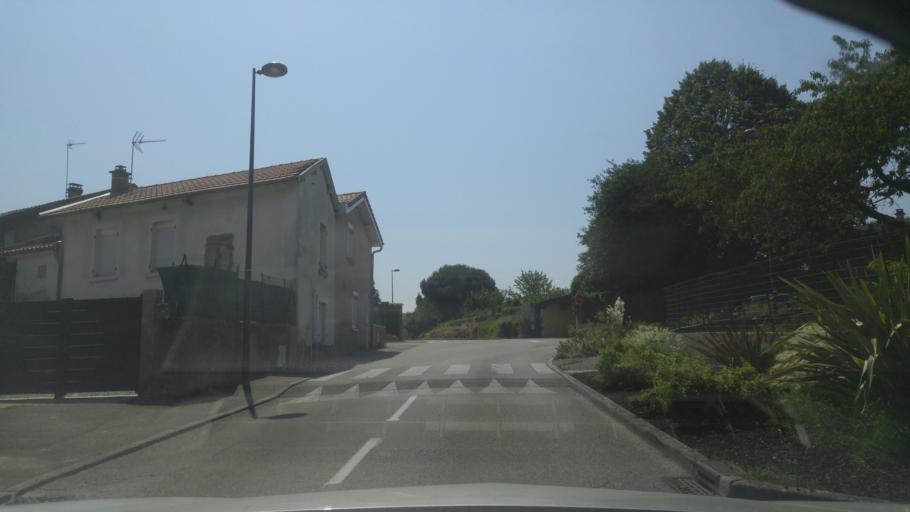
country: FR
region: Rhone-Alpes
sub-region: Departement de l'Isere
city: Tignieu-Jameyzieu
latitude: 45.7393
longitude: 5.1802
